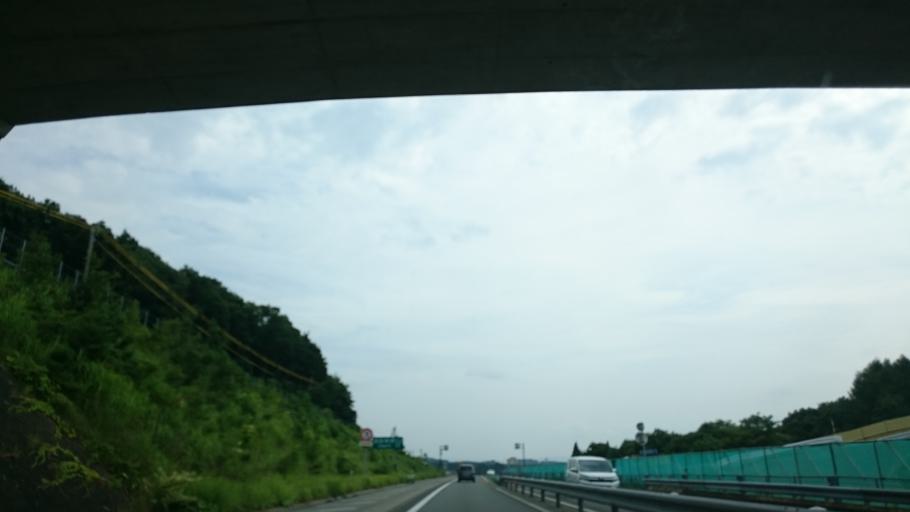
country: JP
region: Gifu
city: Gujo
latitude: 36.0070
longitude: 136.9289
